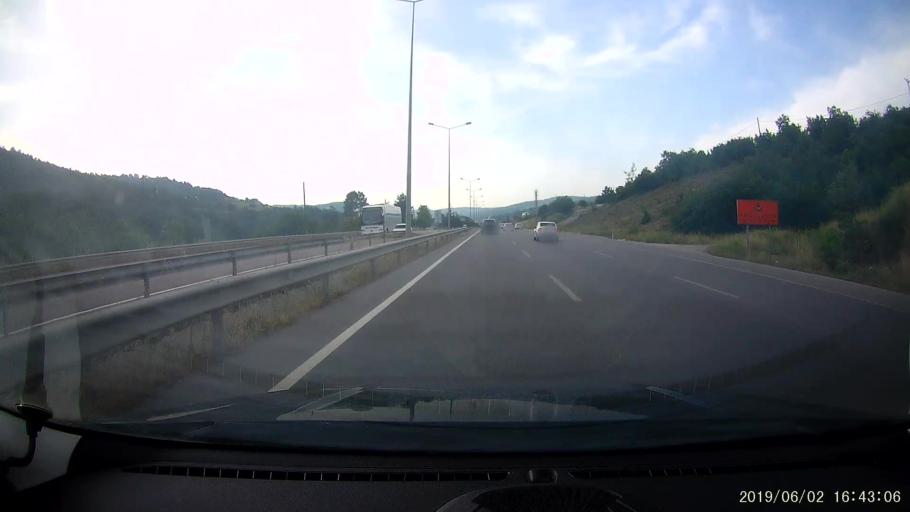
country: TR
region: Samsun
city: Kavak
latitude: 41.1299
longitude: 36.1337
